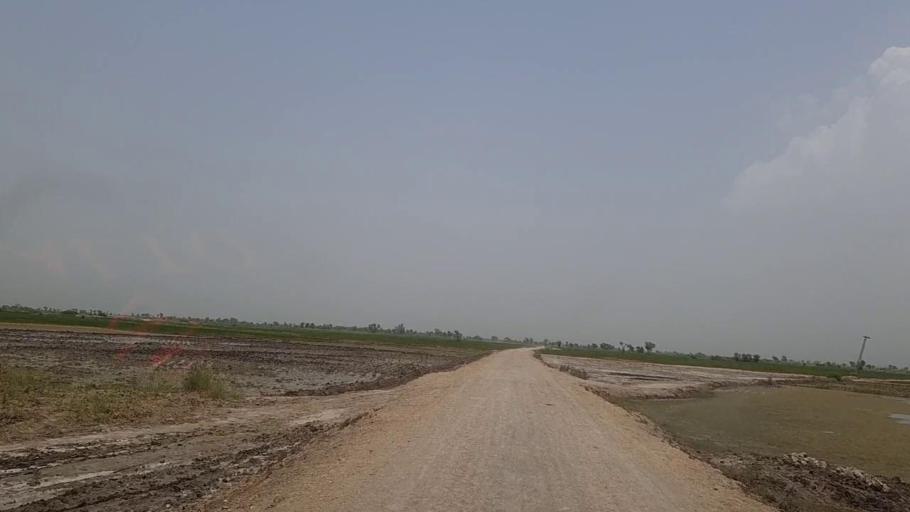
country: PK
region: Sindh
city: Sita Road
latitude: 27.0715
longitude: 67.8660
